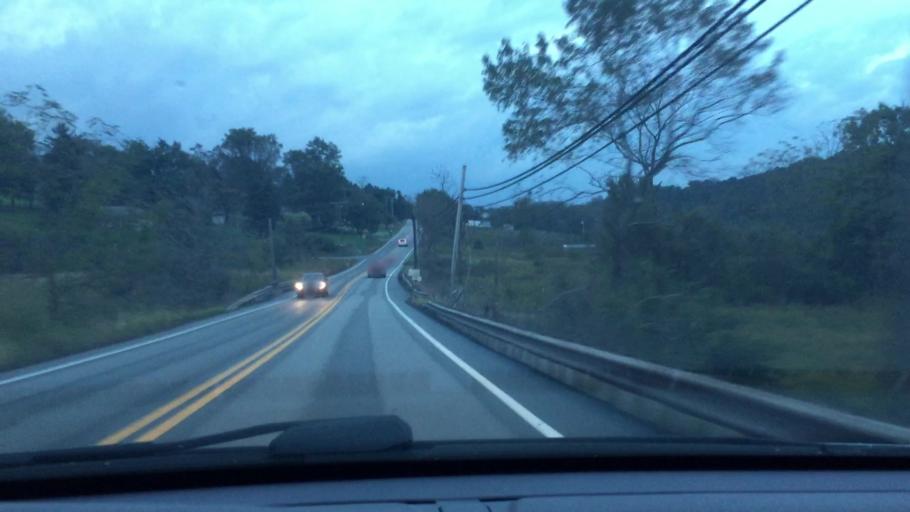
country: US
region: Pennsylvania
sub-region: Washington County
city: McGovern
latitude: 40.1843
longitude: -80.1661
